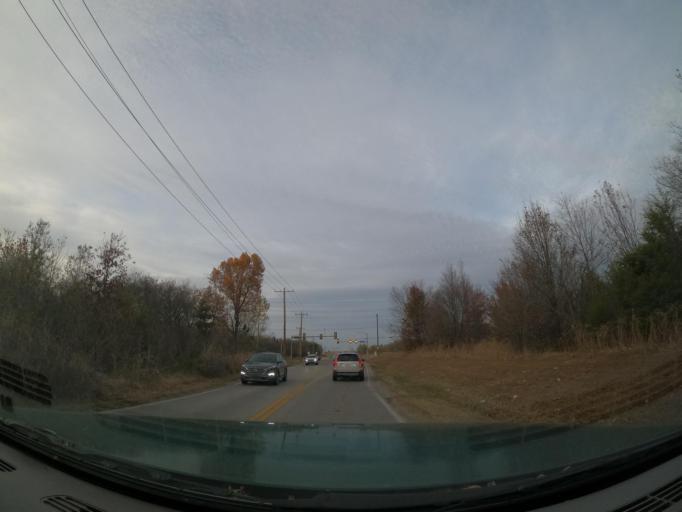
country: US
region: Oklahoma
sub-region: Tulsa County
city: Broken Arrow
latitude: 35.9875
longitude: -95.8153
